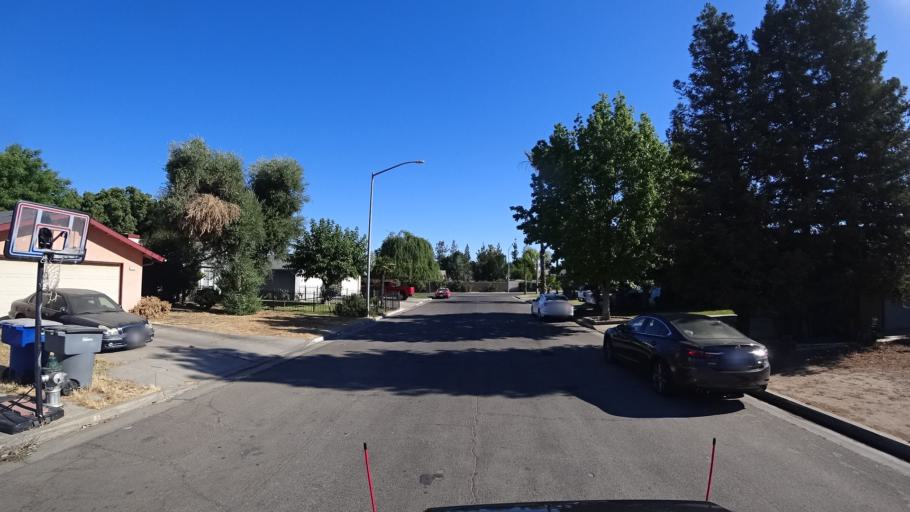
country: US
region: California
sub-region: Fresno County
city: West Park
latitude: 36.7773
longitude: -119.8584
